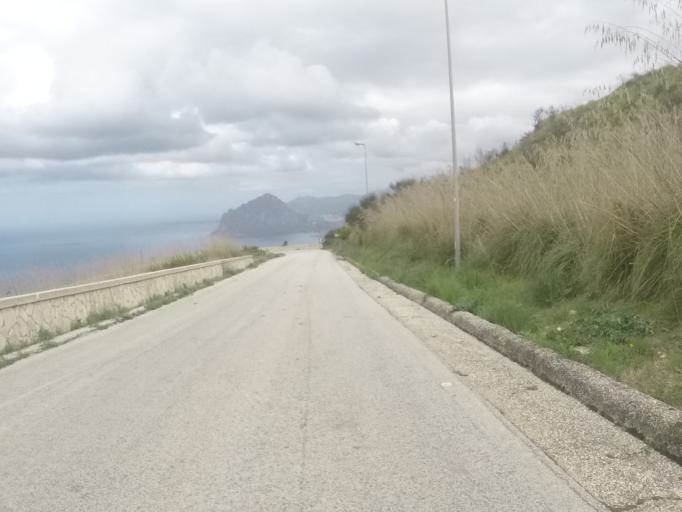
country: IT
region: Sicily
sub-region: Trapani
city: Erice
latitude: 38.0480
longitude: 12.5803
